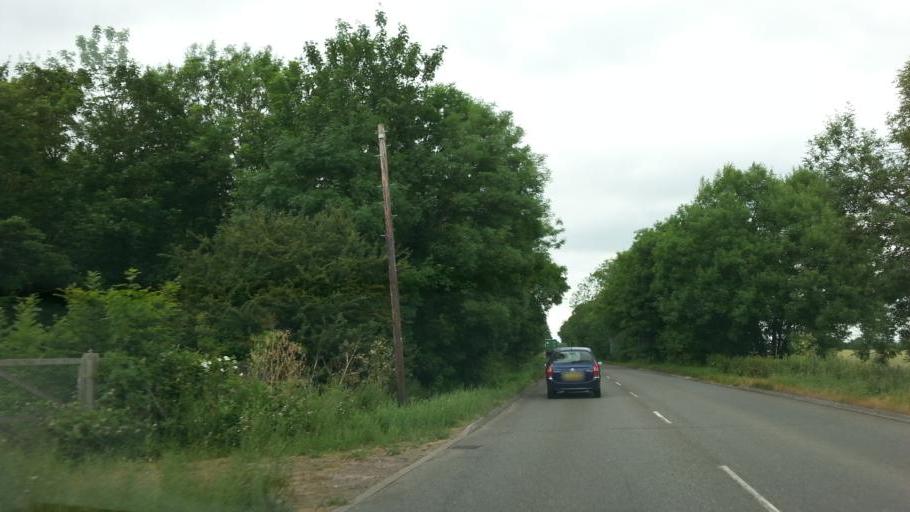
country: GB
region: England
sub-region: Cambridgeshire
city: Papworth Everard
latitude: 52.2581
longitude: -0.1244
